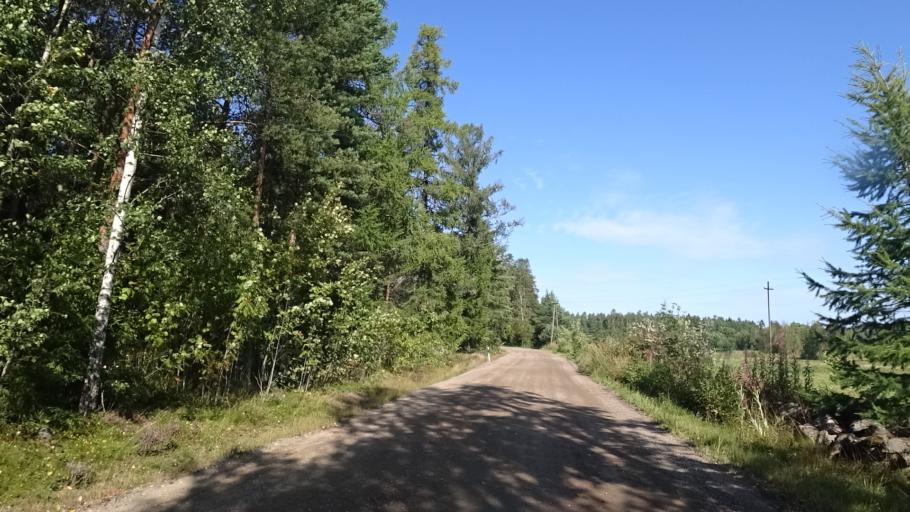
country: FI
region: Kymenlaakso
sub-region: Kotka-Hamina
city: Hamina
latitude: 60.5434
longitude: 27.2189
